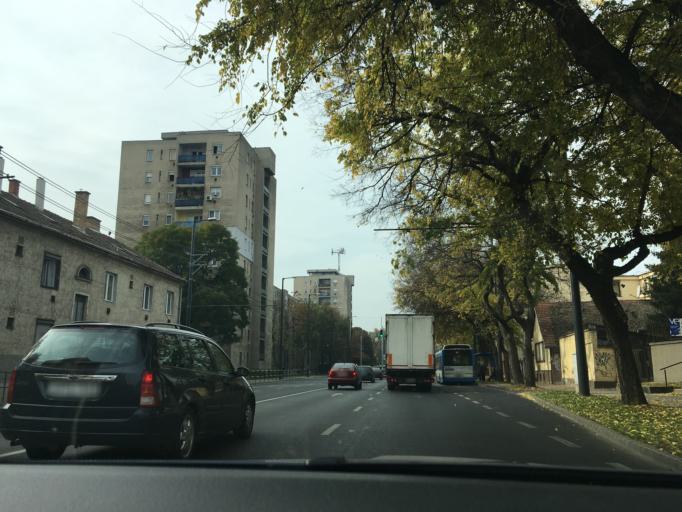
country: HU
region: Hajdu-Bihar
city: Debrecen
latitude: 47.5217
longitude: 21.6238
